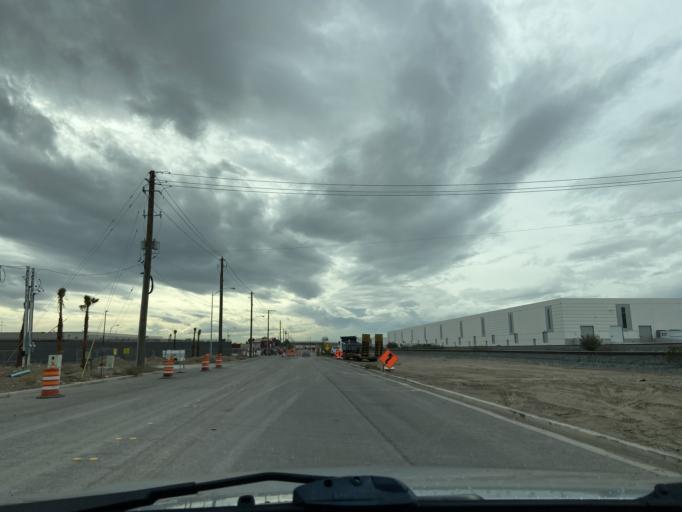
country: US
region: Nevada
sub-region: Clark County
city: Nellis Air Force Base
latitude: 36.2467
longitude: -115.0998
